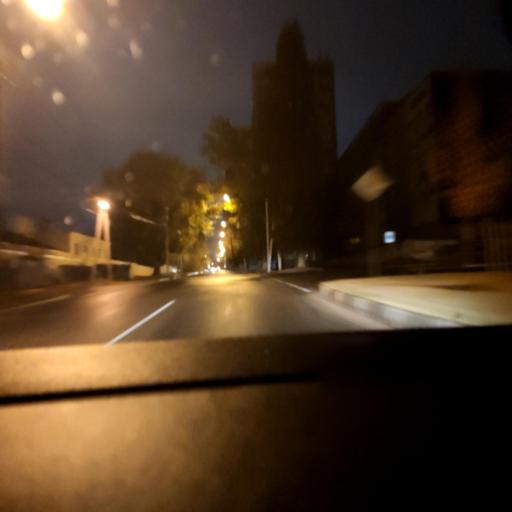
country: RU
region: Voronezj
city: Voronezh
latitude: 51.6913
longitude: 39.1903
